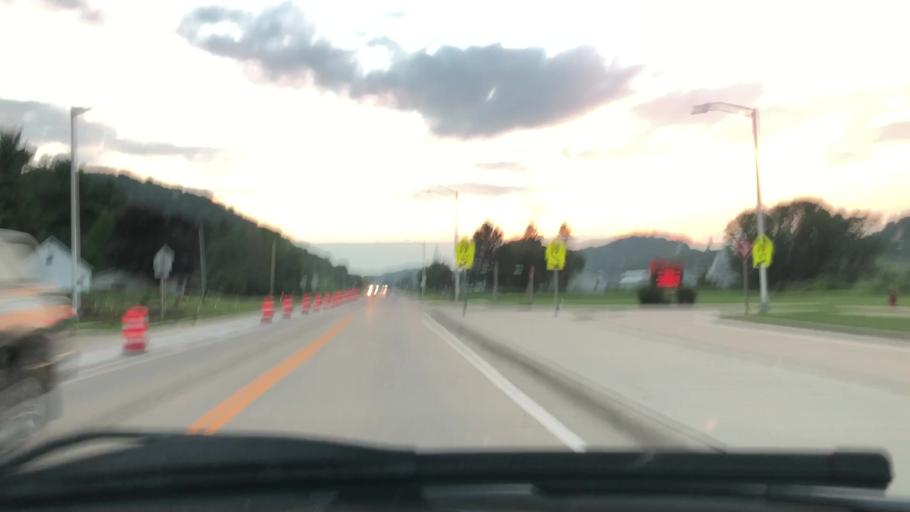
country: US
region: Wisconsin
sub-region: Richland County
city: Richland Center
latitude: 43.3444
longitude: -90.4023
